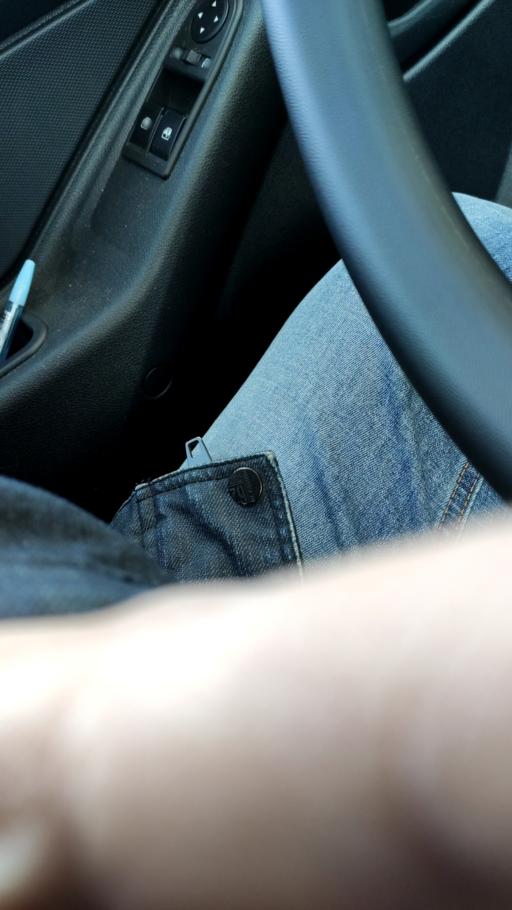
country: RU
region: Voronezj
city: Ramon'
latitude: 51.9112
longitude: 39.3288
